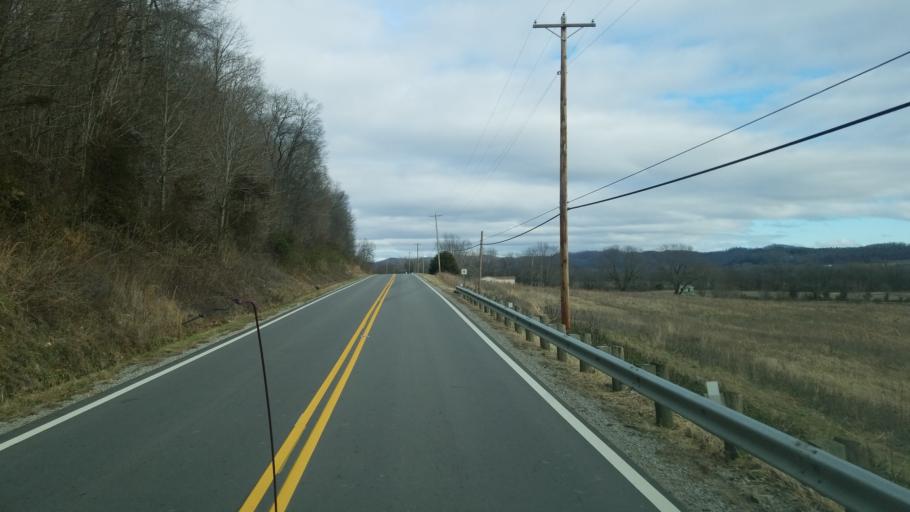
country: US
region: Kentucky
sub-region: Lewis County
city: Vanceburg
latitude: 38.6235
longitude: -83.1718
